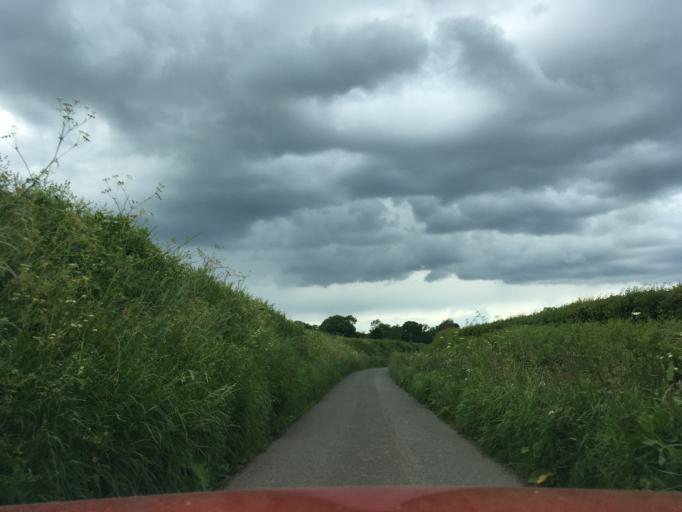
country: GB
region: England
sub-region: Wiltshire
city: Hankerton
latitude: 51.6516
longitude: -2.0182
